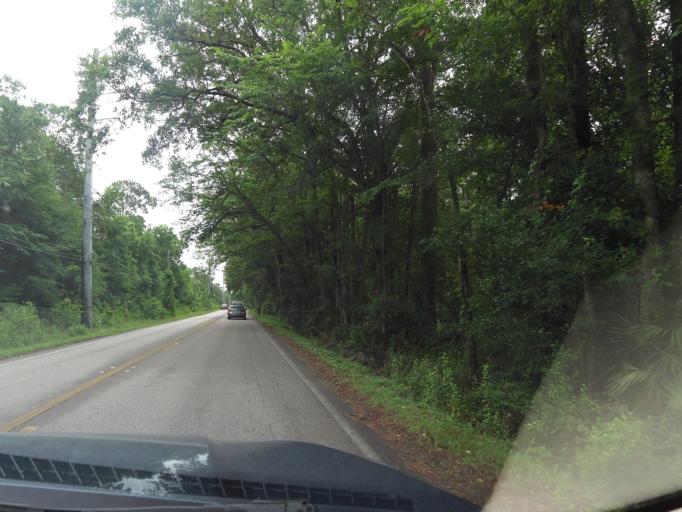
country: US
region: Florida
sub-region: Saint Johns County
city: Saint Augustine
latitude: 29.9142
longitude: -81.3707
